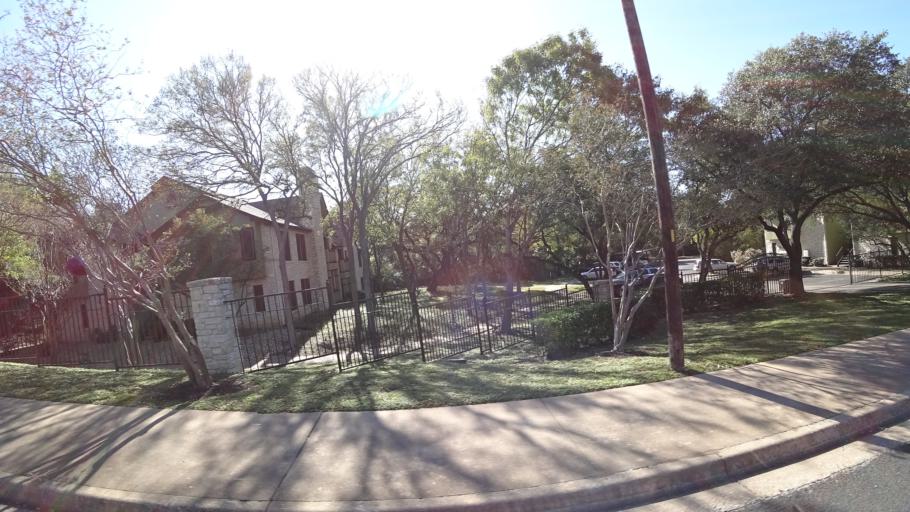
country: US
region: Texas
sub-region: Williamson County
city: Jollyville
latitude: 30.4099
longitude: -97.7507
